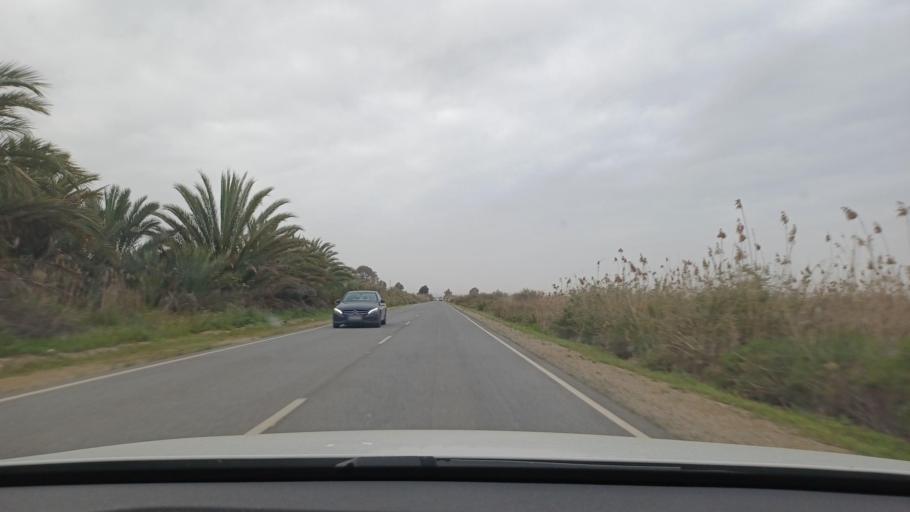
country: ES
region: Valencia
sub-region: Provincia de Alicante
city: Dolores
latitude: 38.1752
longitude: -0.7019
